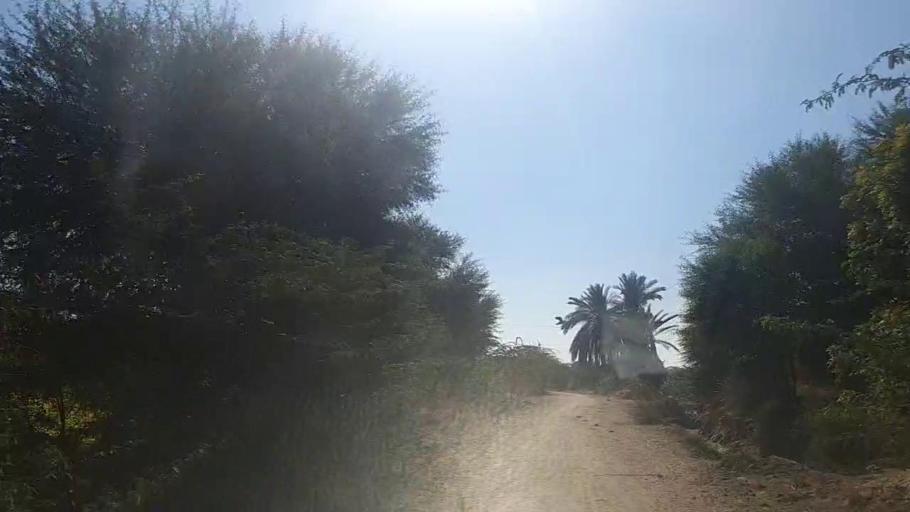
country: PK
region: Sindh
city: Khadro
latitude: 26.1546
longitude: 68.8379
